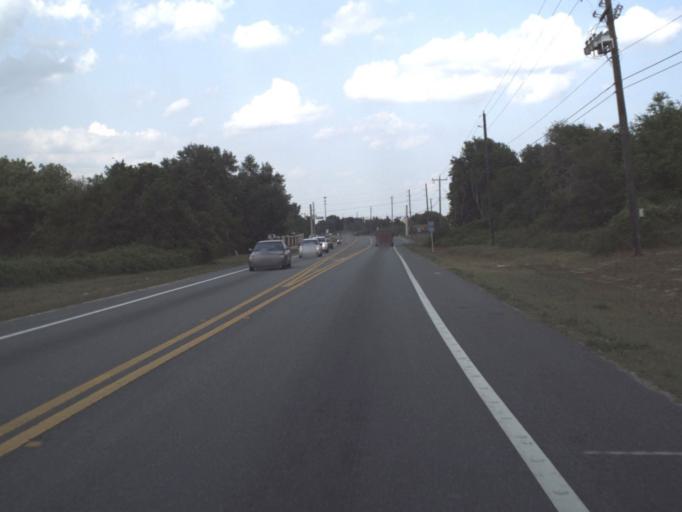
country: US
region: Florida
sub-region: Lake County
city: Howie In The Hills
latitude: 28.7628
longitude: -81.7559
